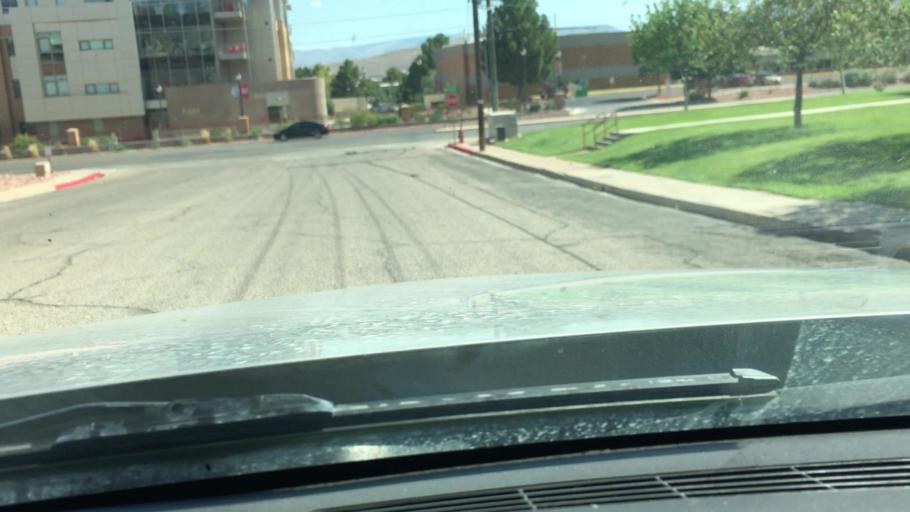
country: US
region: Utah
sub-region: Washington County
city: Saint George
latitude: 37.1070
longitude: -113.5643
